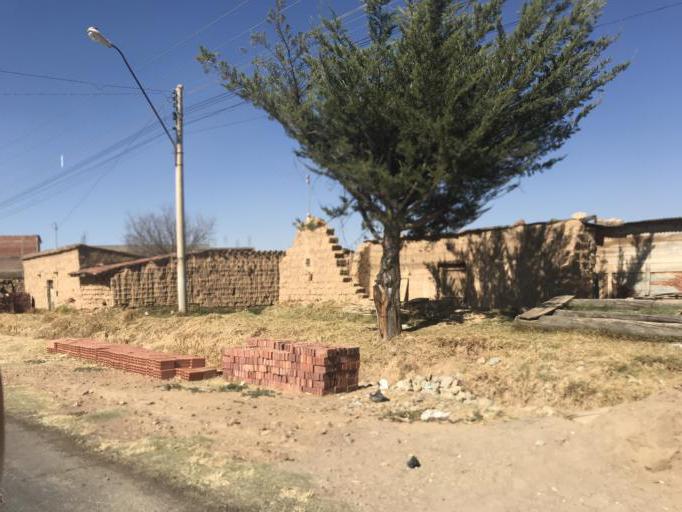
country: BO
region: Cochabamba
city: Cliza
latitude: -17.5732
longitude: -65.9003
